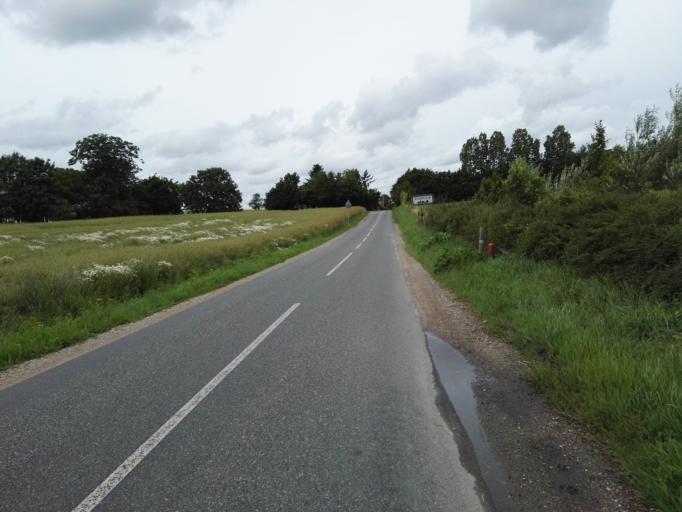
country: DK
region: Capital Region
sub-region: Egedal Kommune
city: Stenlose
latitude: 55.7880
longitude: 12.2041
